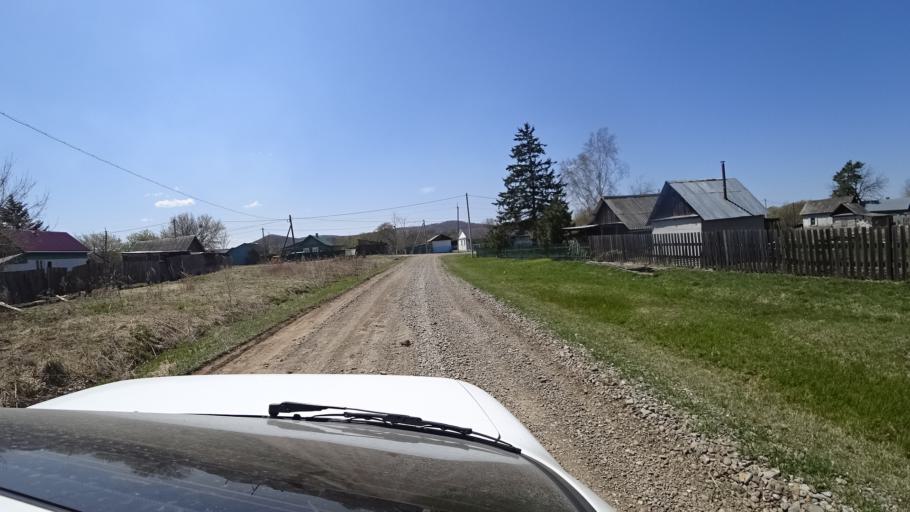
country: RU
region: Primorskiy
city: Lazo
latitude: 45.7935
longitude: 133.7645
